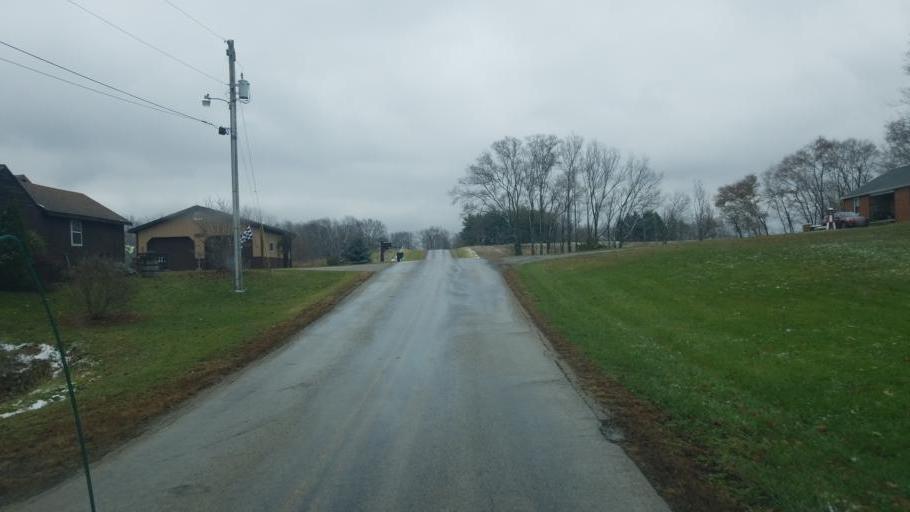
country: US
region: Ohio
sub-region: Richland County
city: Shelby
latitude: 40.9041
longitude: -82.5658
